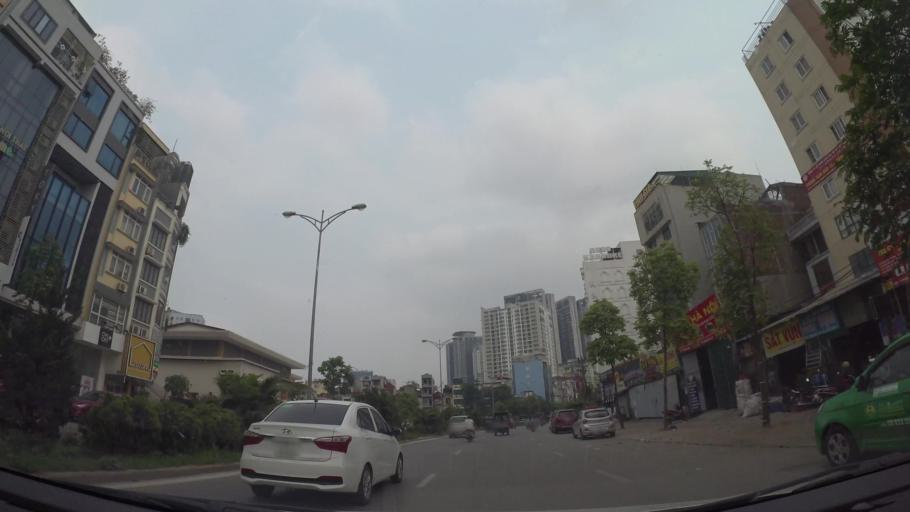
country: VN
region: Ha Noi
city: Cau Dien
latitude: 21.0326
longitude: 105.7730
